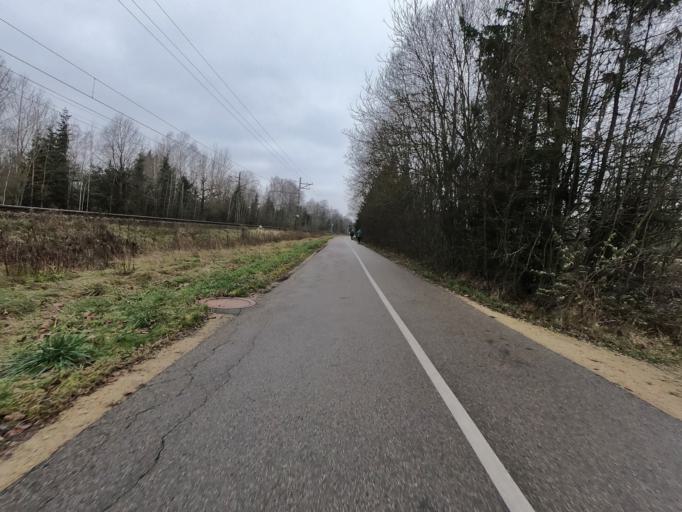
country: LV
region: Babite
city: Pinki
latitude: 56.9514
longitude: 23.9831
